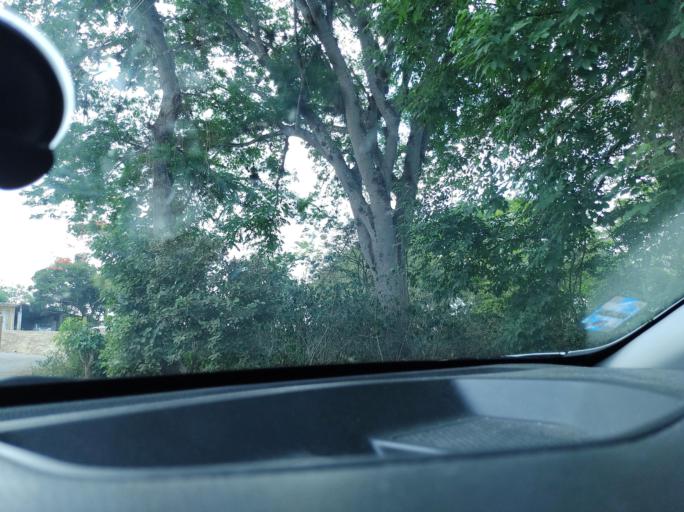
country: MX
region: Veracruz
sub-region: Coatepec
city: Bella Esperanza
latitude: 19.4330
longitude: -96.8647
